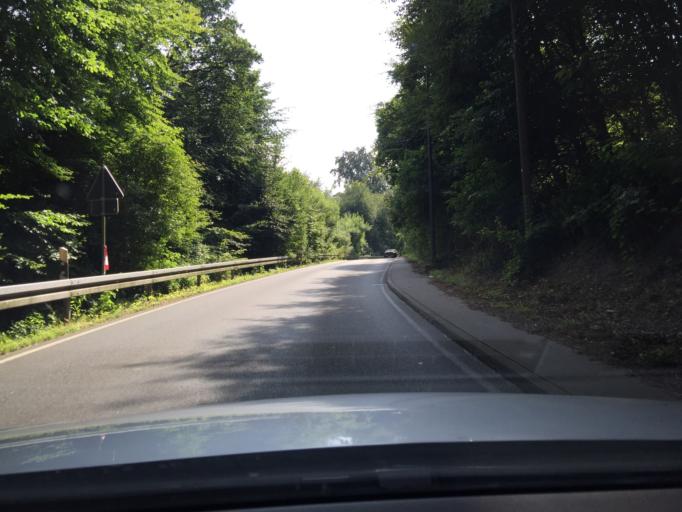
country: DE
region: North Rhine-Westphalia
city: Hattingen
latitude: 51.3669
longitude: 7.1234
